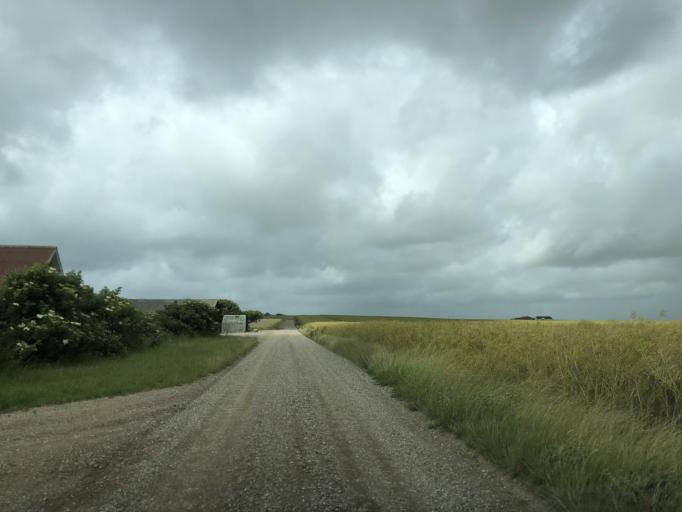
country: DK
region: Central Jutland
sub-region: Lemvig Kommune
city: Harboore
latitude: 56.5012
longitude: 8.1284
